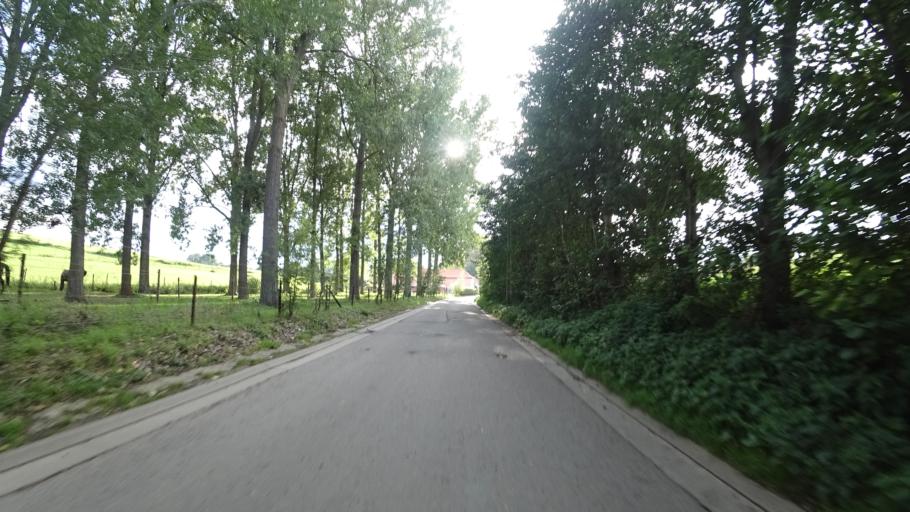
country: BE
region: Wallonia
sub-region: Province du Brabant Wallon
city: Waterloo
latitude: 50.6801
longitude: 4.4389
